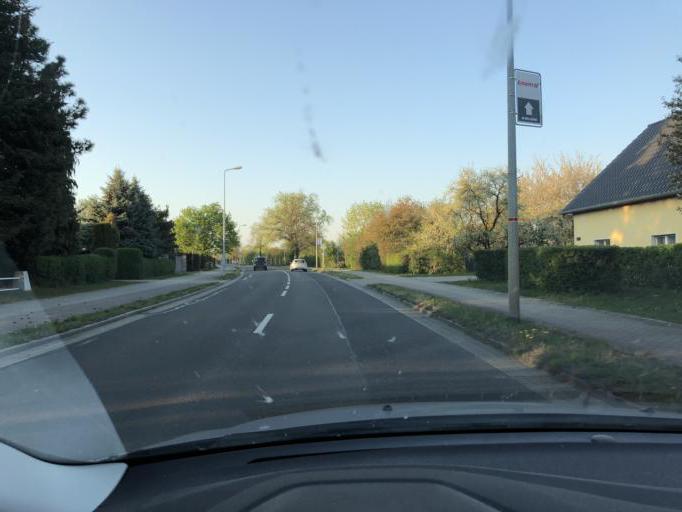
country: DE
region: Brandenburg
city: Spremberg
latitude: 51.5342
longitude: 14.3409
